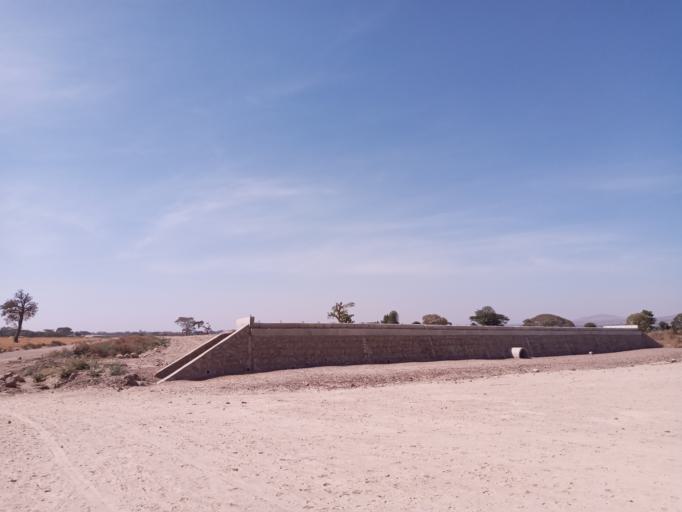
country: ET
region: Oromiya
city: Shashemene
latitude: 7.3864
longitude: 38.6507
